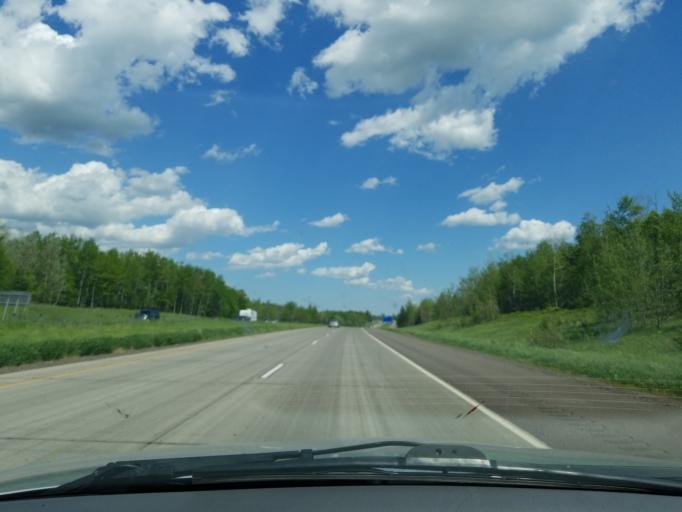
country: US
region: Minnesota
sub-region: Carlton County
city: Esko
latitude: 46.6988
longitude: -92.3848
